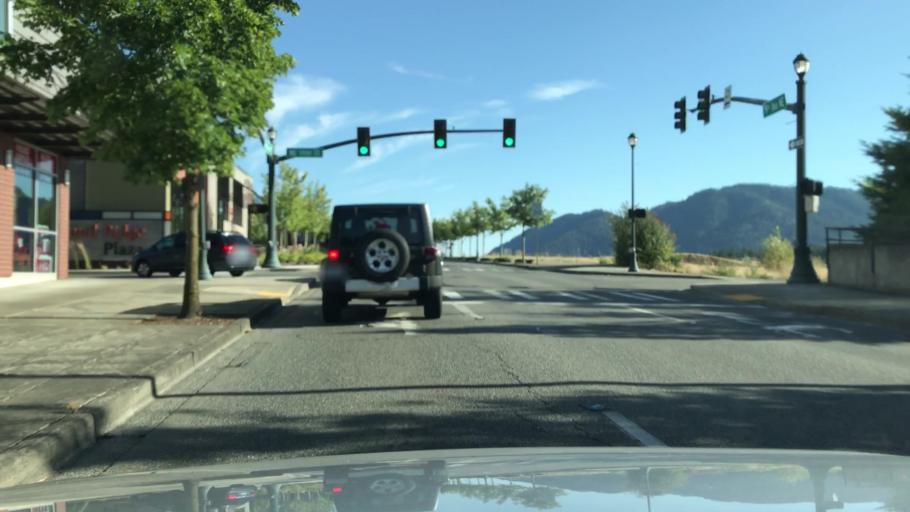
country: US
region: Washington
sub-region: King County
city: Issaquah
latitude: 47.5447
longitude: -122.0201
